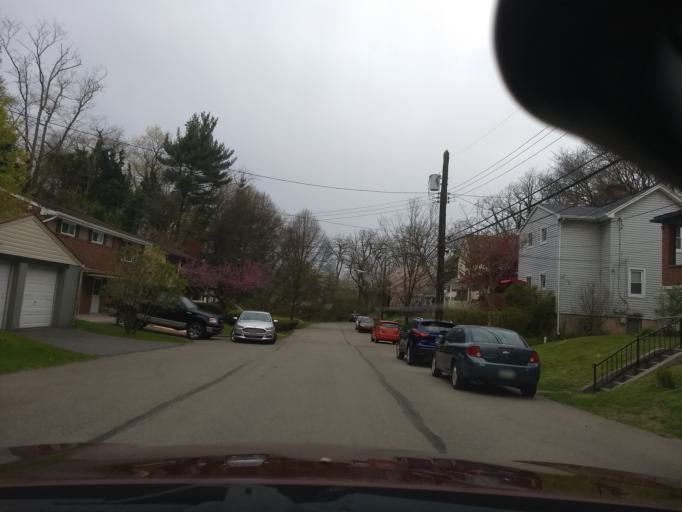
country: US
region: Pennsylvania
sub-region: Allegheny County
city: Ingram
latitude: 40.4419
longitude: -80.0643
